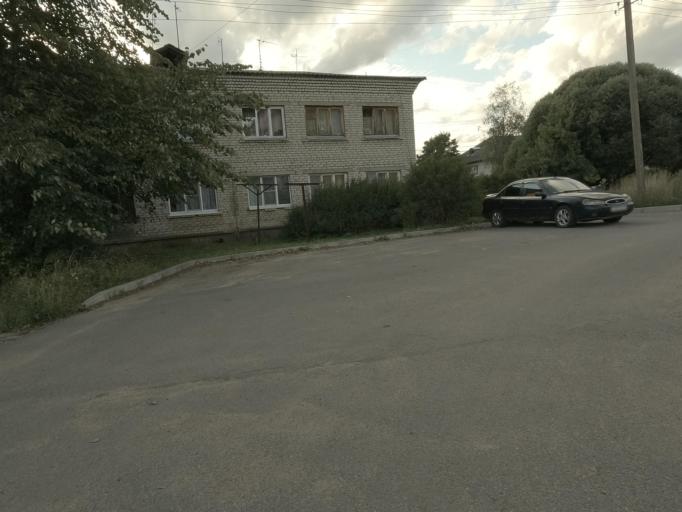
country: RU
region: Leningrad
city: Mga
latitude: 59.7520
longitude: 31.0386
